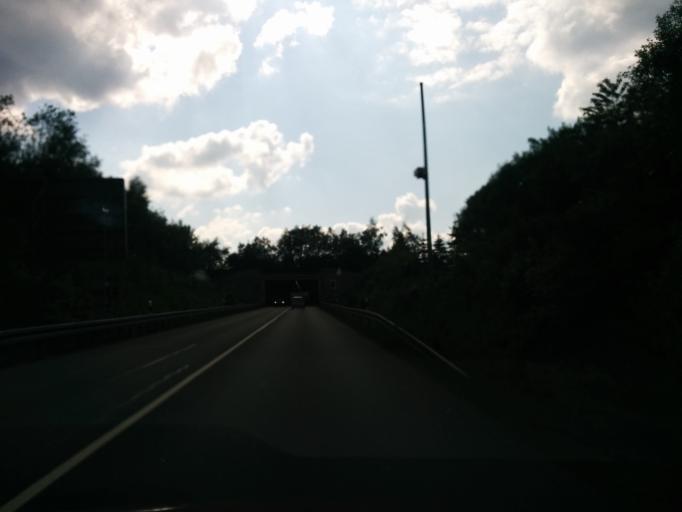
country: DE
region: Lower Saxony
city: Braunlage
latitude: 51.7137
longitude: 10.6203
